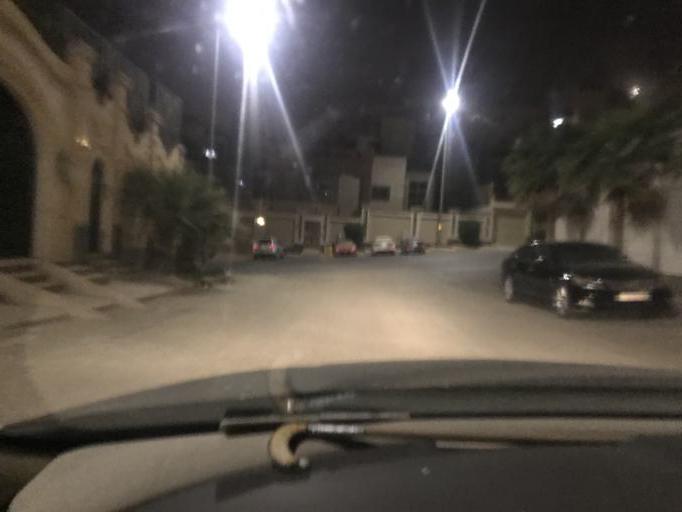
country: SA
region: Ar Riyad
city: Riyadh
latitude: 24.7754
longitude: 46.6917
